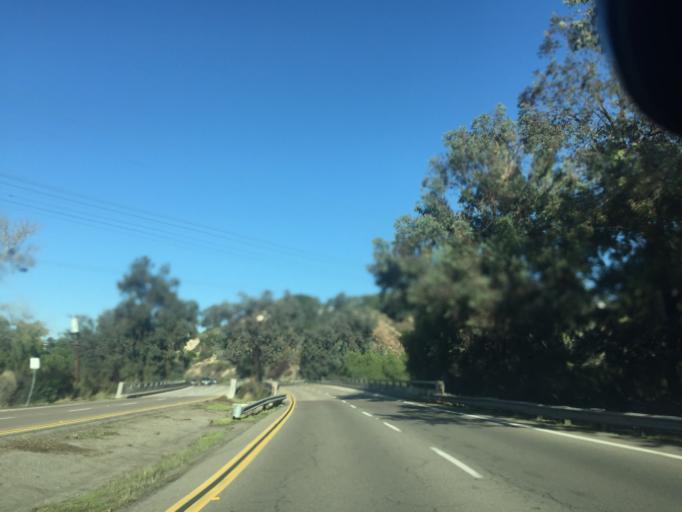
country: US
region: California
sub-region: San Diego County
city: Lemon Grove
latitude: 32.7620
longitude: -117.0980
